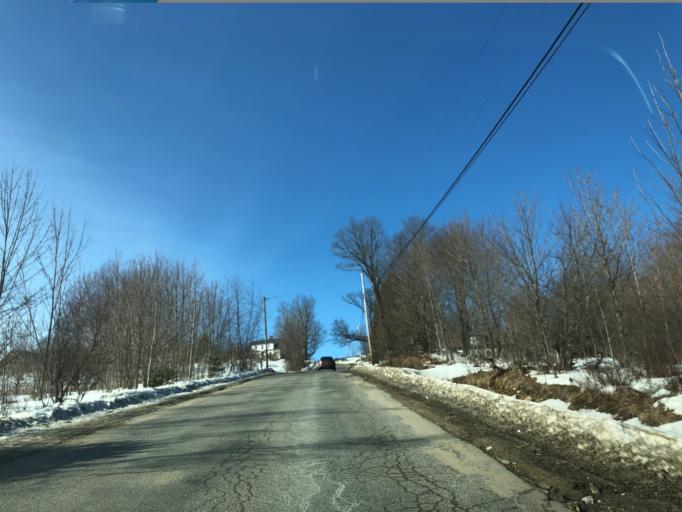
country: US
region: Maine
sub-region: Oxford County
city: Buckfield
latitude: 44.2641
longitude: -70.3454
